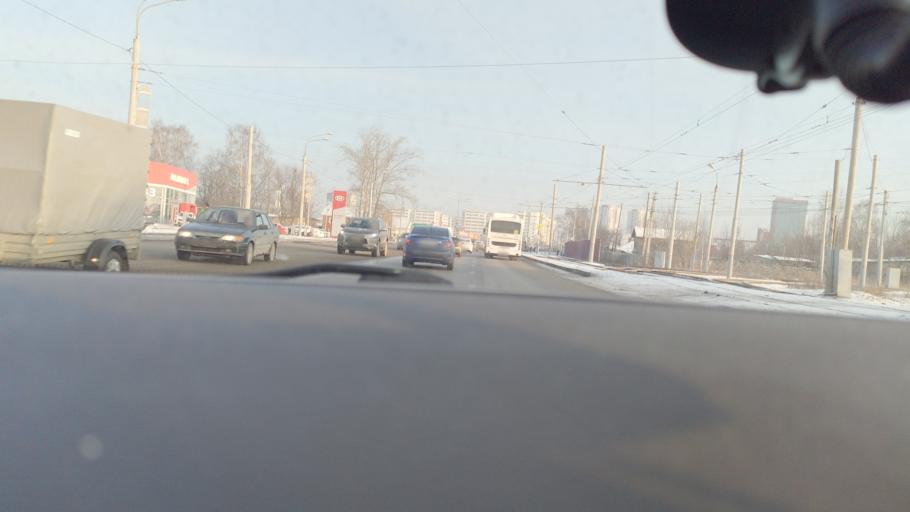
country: RU
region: Perm
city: Kondratovo
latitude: 57.9627
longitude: 56.1392
